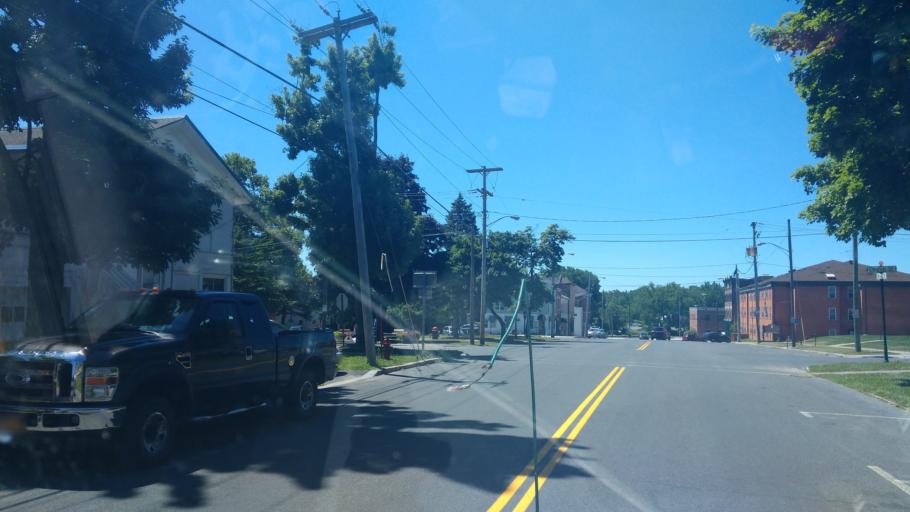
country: US
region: New York
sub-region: Wayne County
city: Lyons
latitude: 43.0641
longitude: -76.9940
